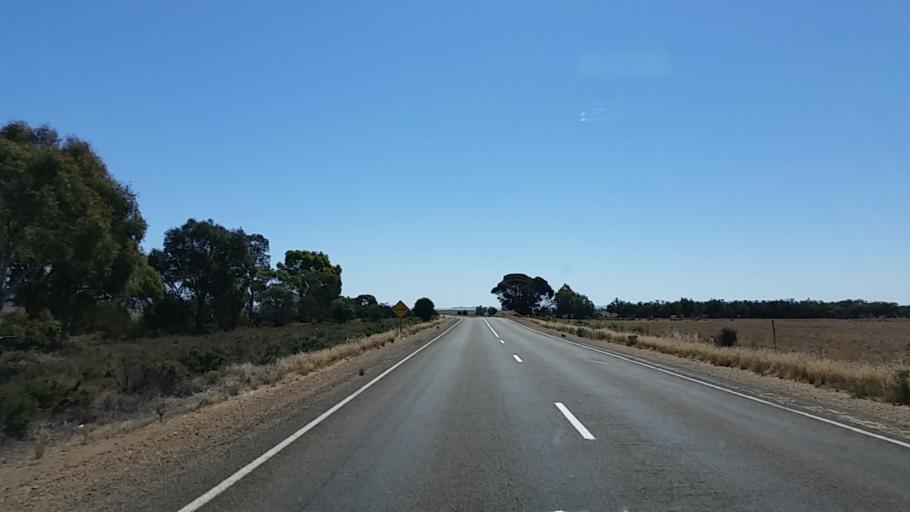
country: AU
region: South Australia
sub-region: Peterborough
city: Peterborough
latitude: -32.7654
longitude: 138.6567
